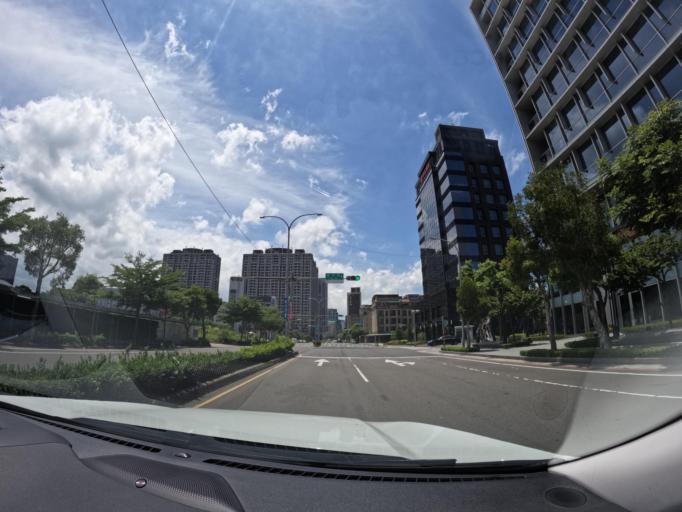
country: TW
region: Taipei
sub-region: Taipei
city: Banqiao
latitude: 25.0885
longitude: 121.3802
